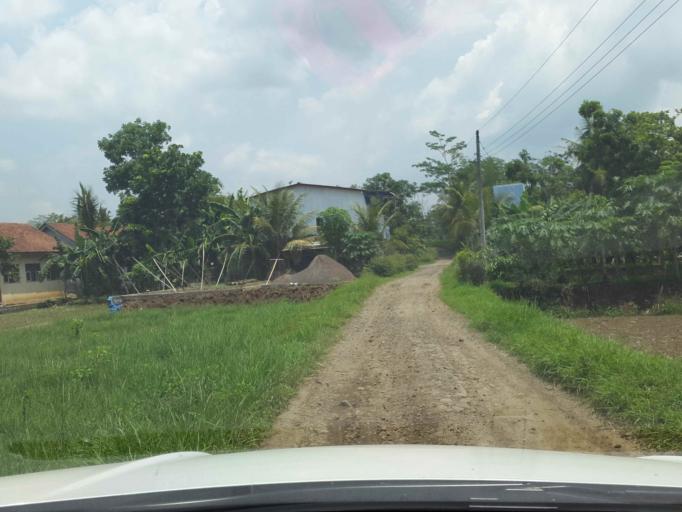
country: ID
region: West Java
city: Cintaratu
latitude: -7.3653
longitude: 108.6832
